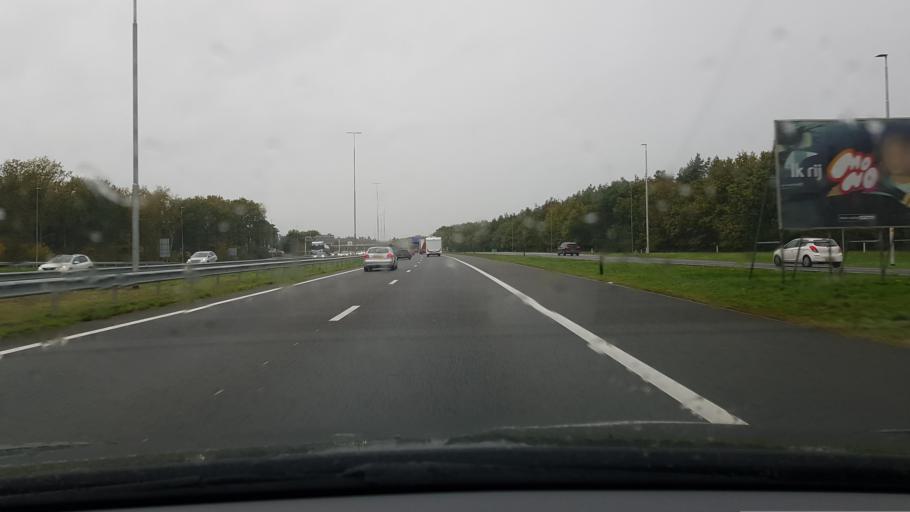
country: NL
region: North Holland
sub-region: Gemeente Laren
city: Laren
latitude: 52.2348
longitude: 5.2316
